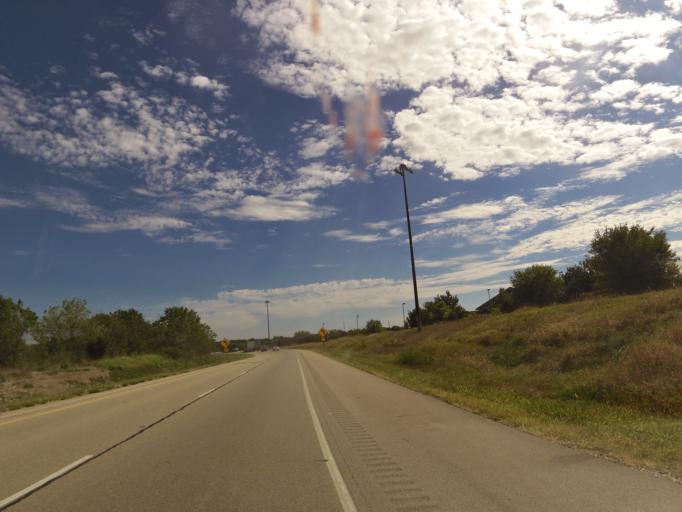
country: US
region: Illinois
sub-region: McLean County
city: Normal
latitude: 40.5374
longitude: -89.0126
